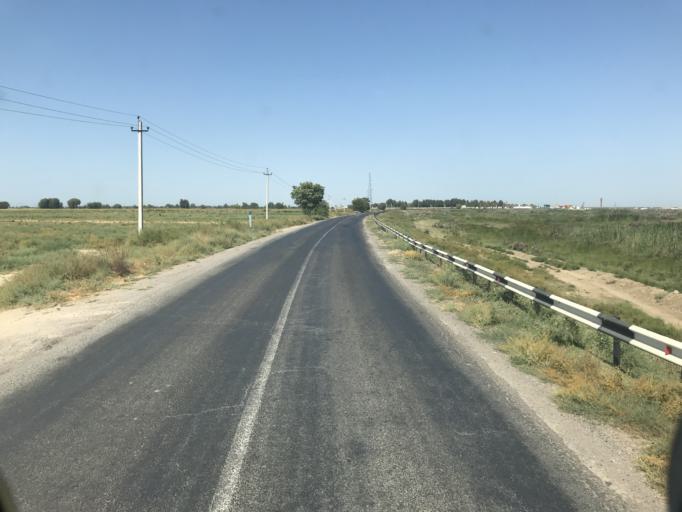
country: KZ
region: Ongtustik Qazaqstan
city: Ilyich
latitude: 40.9508
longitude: 68.4745
